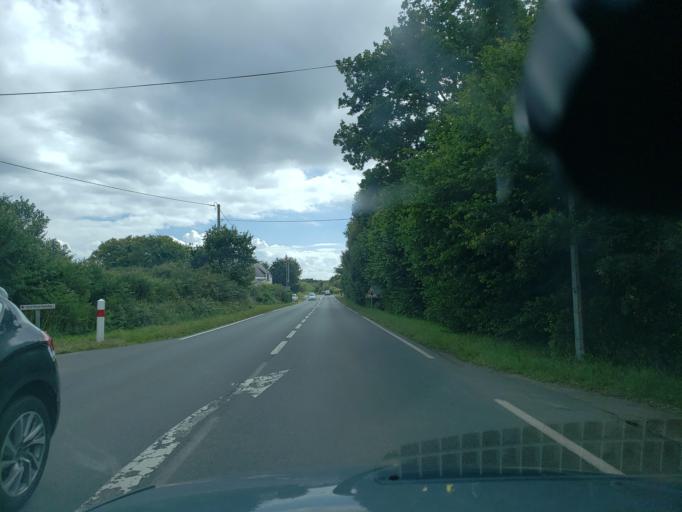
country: FR
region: Brittany
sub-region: Departement du Finistere
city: Plomeur
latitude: 47.8320
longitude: -4.2885
